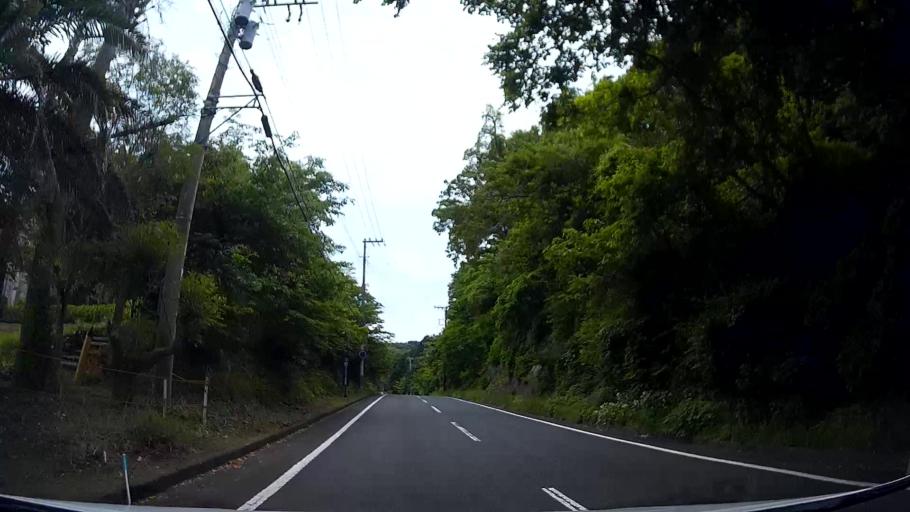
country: JP
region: Shizuoka
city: Ito
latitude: 34.9430
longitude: 139.1370
